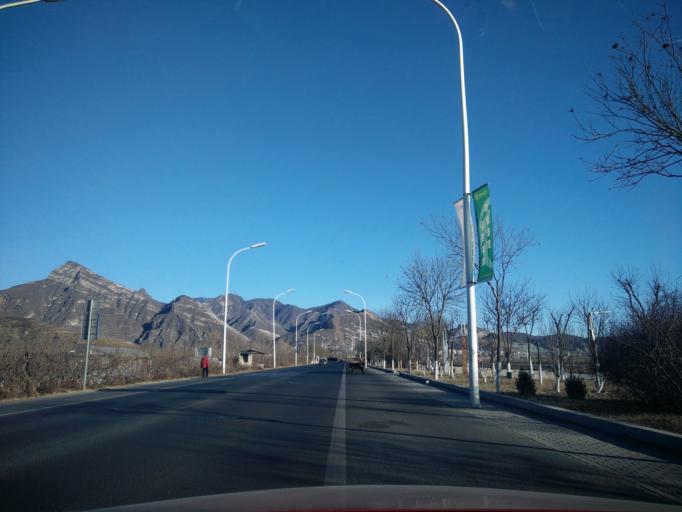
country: CN
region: Beijing
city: Junzhuang
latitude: 39.9863
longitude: 116.0808
